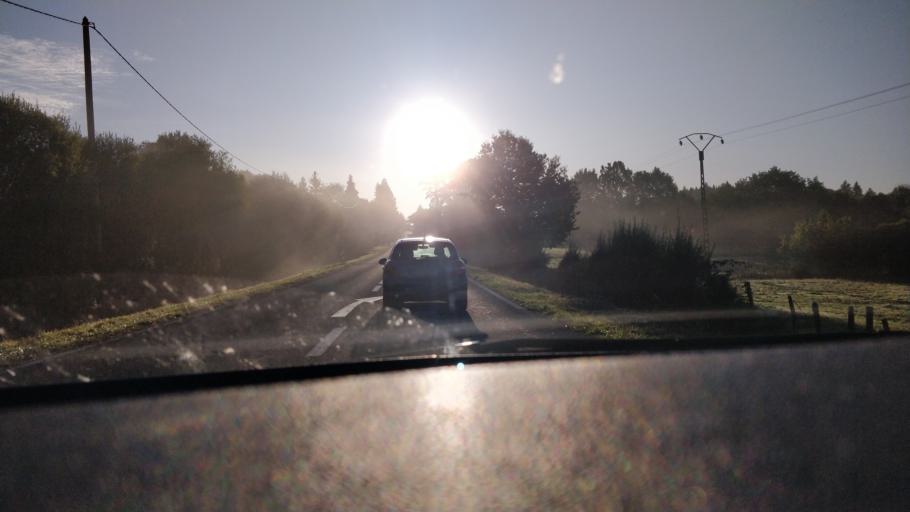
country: FR
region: Limousin
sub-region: Departement de la Creuse
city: Bourganeuf
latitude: 45.9481
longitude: 1.6965
